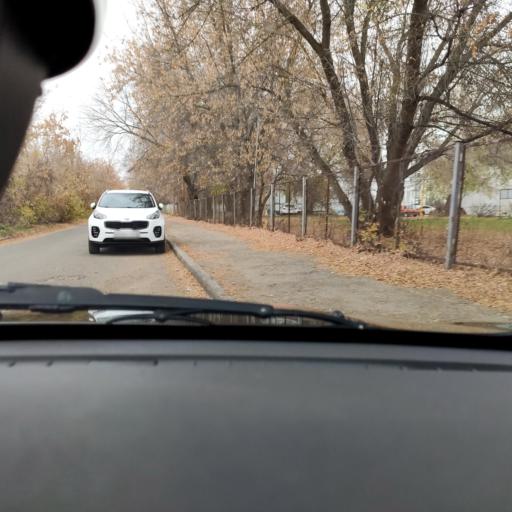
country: RU
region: Samara
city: Tol'yatti
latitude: 53.5275
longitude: 49.3915
